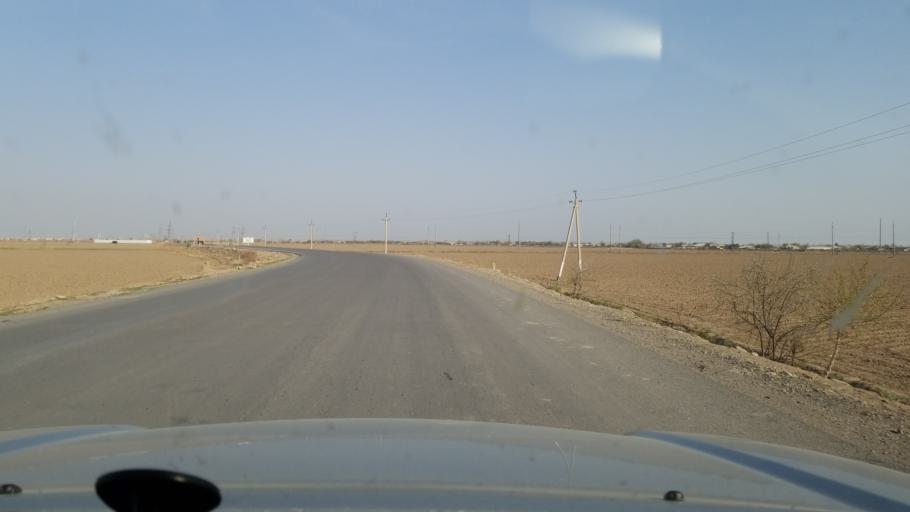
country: AF
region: Jowzjan
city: Khamyab
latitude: 37.6070
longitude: 65.7331
